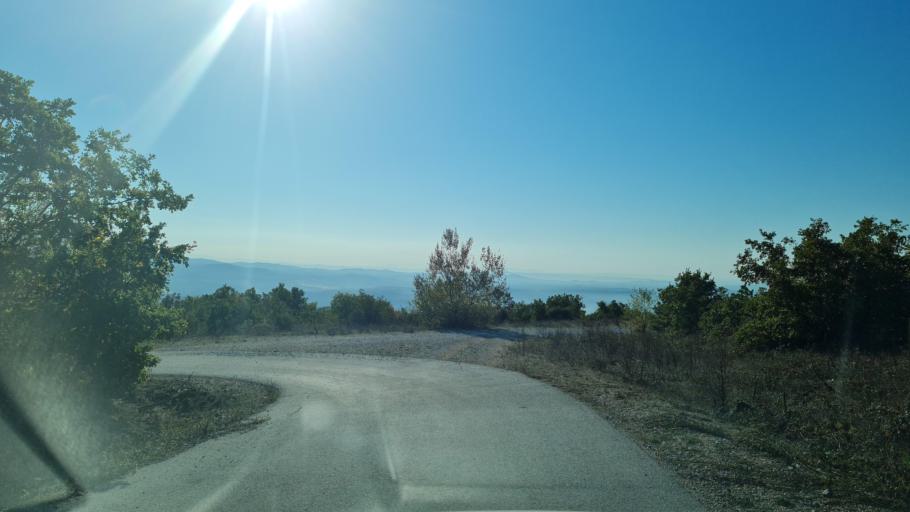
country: MK
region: Bogdanci
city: Bogdanci
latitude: 41.2292
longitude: 22.5600
